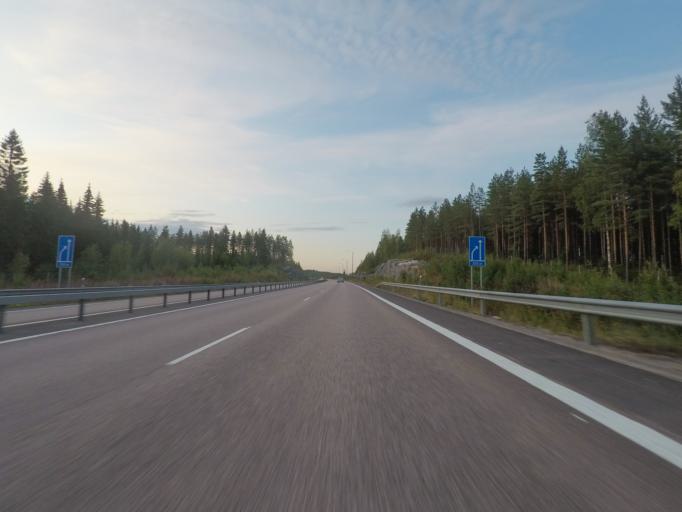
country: FI
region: Central Finland
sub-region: Jyvaeskylae
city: Saeynaetsalo
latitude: 62.1678
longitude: 25.9038
